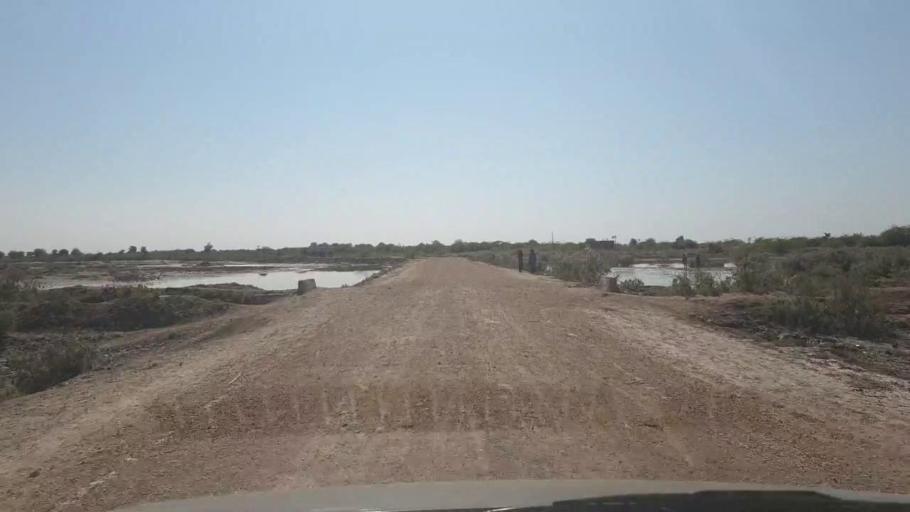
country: PK
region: Sindh
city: Dhoro Naro
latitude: 25.4446
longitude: 69.6105
